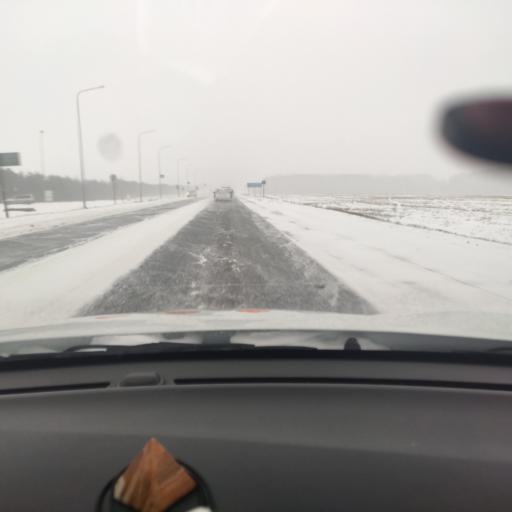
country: RU
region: Tatarstan
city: Verkhniy Uslon
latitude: 55.6600
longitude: 48.8577
